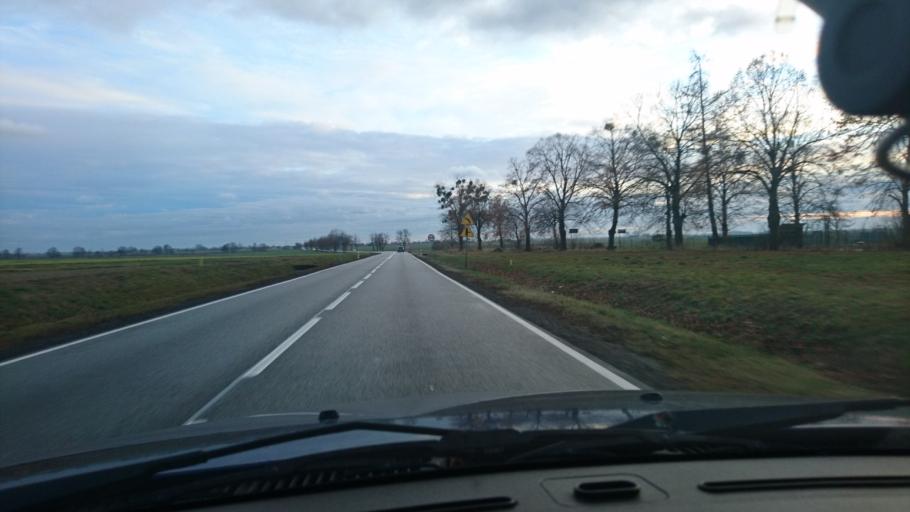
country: PL
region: Opole Voivodeship
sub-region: Powiat kluczborski
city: Kluczbork
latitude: 51.0253
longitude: 18.1928
